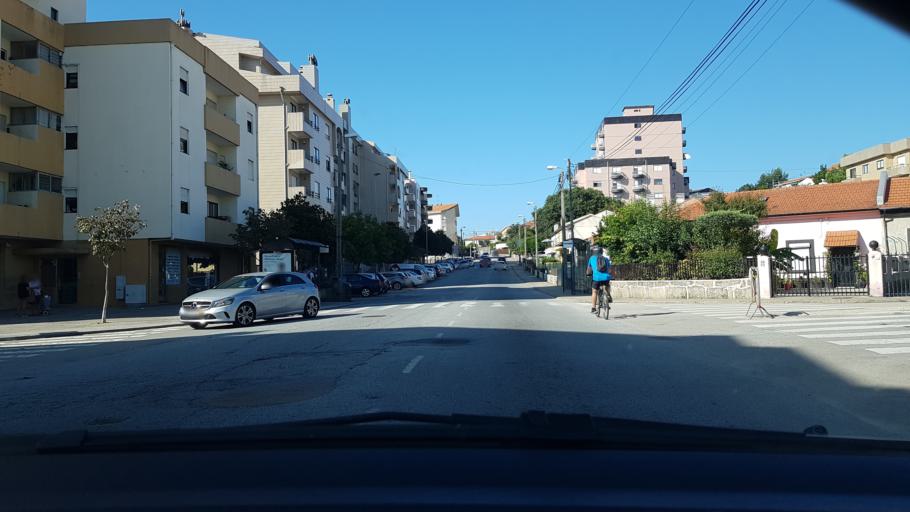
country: PT
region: Porto
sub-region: Gondomar
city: Baguim do Monte
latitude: 41.1857
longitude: -8.5401
